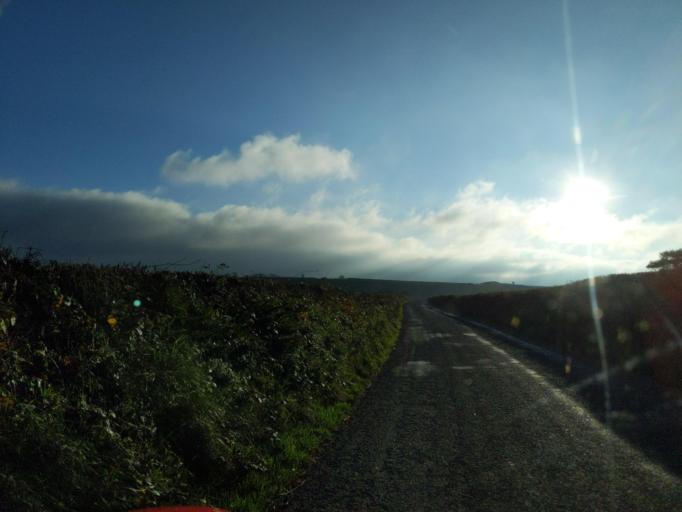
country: GB
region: England
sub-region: Cornwall
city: Pillaton
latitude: 50.4014
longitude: -4.3352
